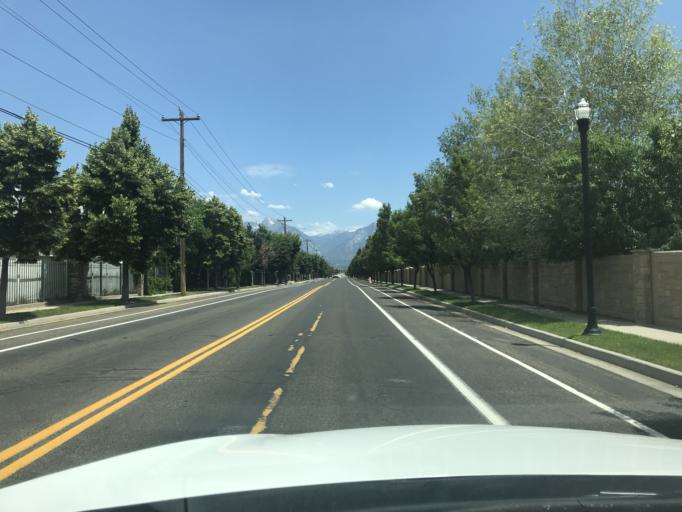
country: US
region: Utah
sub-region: Salt Lake County
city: South Jordan Heights
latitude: 40.5660
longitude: -111.9922
